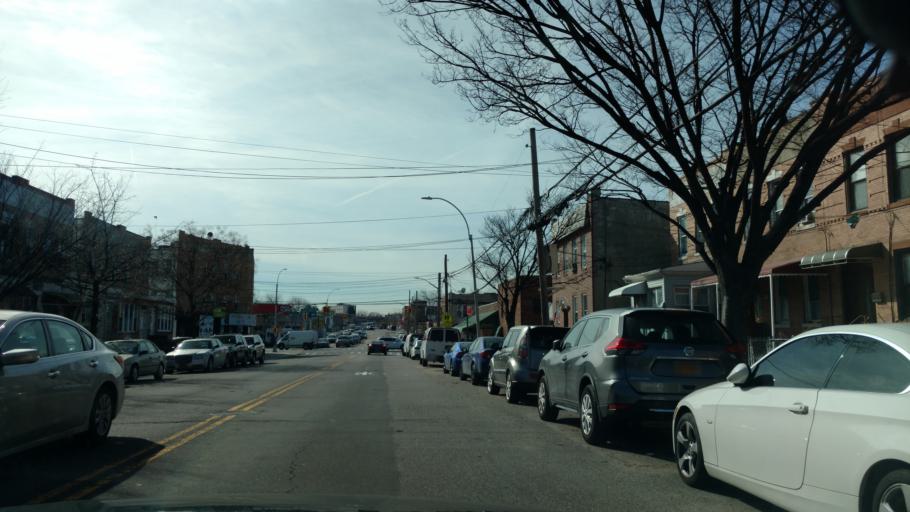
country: US
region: New York
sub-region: Kings County
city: East New York
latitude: 40.7151
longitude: -73.9003
